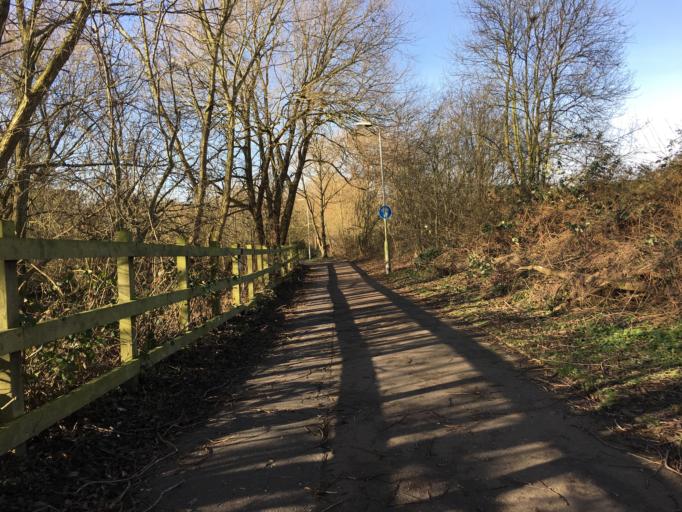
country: GB
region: England
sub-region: Warwickshire
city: Rugby
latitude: 52.3845
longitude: -1.2518
